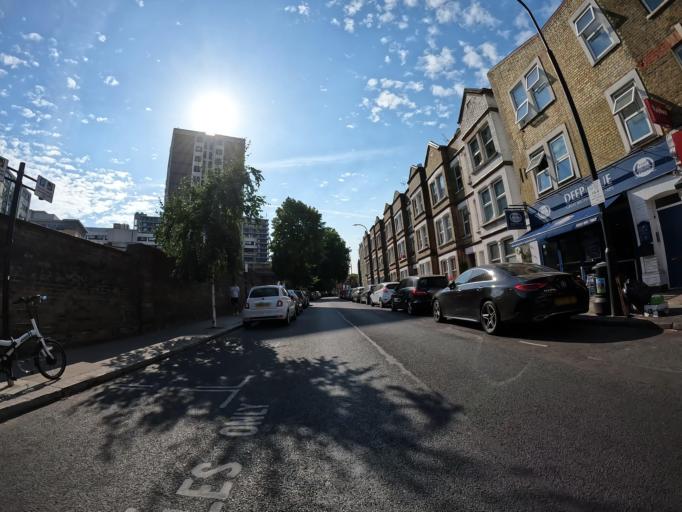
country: GB
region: England
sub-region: Greater London
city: Hendon
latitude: 51.5847
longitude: -0.2186
